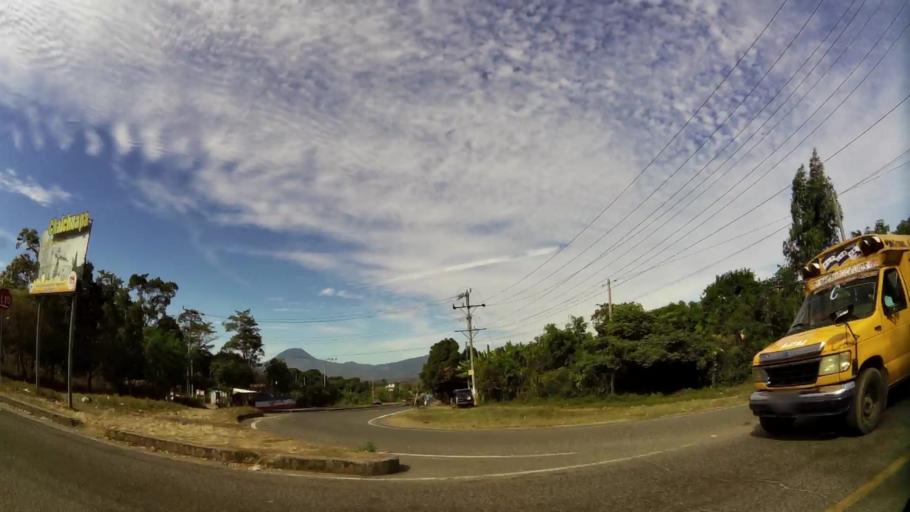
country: SV
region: Santa Ana
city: Chalchuapa
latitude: 13.9774
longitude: -89.6906
